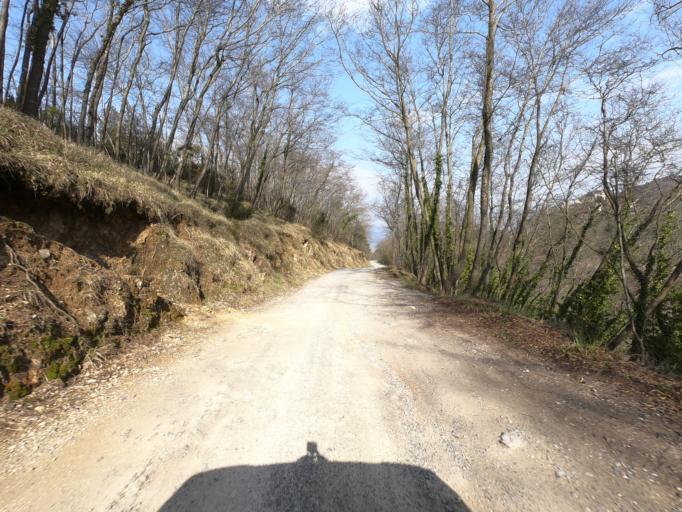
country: IT
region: Liguria
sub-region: Provincia di Savona
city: Balestrino
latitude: 44.1146
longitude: 8.1463
